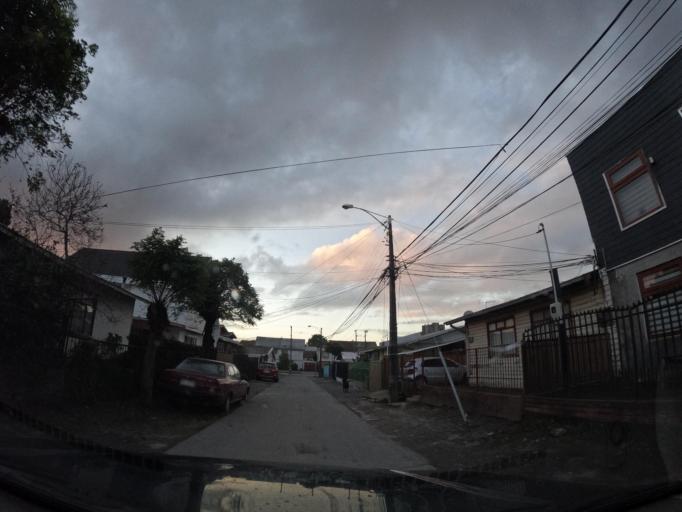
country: CL
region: Biobio
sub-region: Provincia de Concepcion
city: Chiguayante
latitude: -36.9262
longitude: -73.0278
